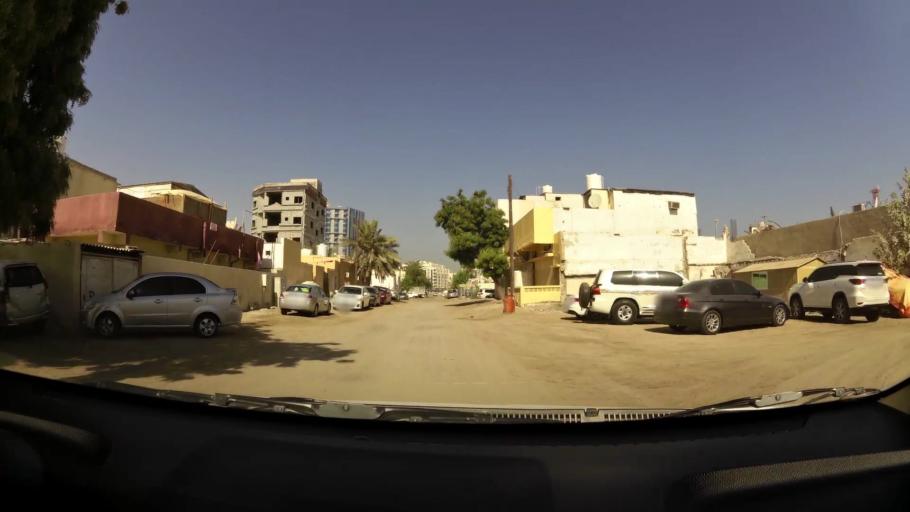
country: AE
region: Ajman
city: Ajman
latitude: 25.4110
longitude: 55.4489
